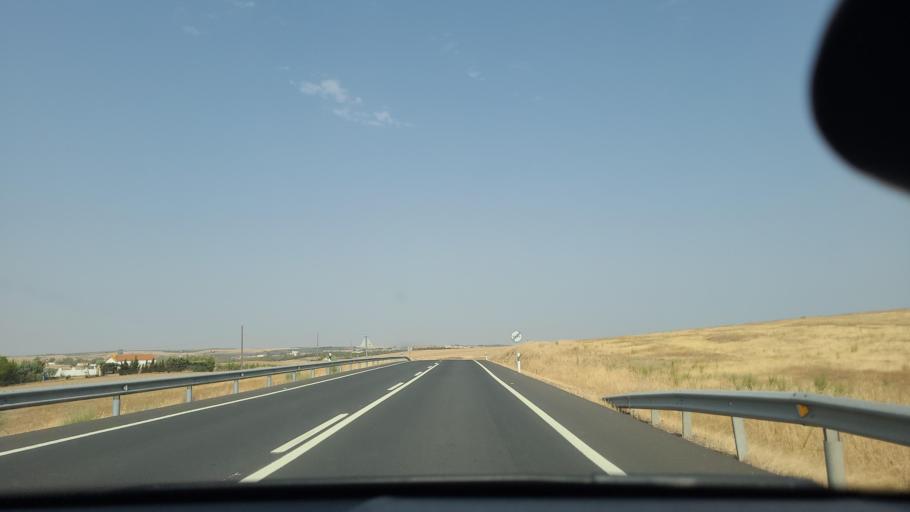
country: ES
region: Extremadura
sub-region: Provincia de Badajoz
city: Berlanga
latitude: 38.2686
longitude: -5.7896
